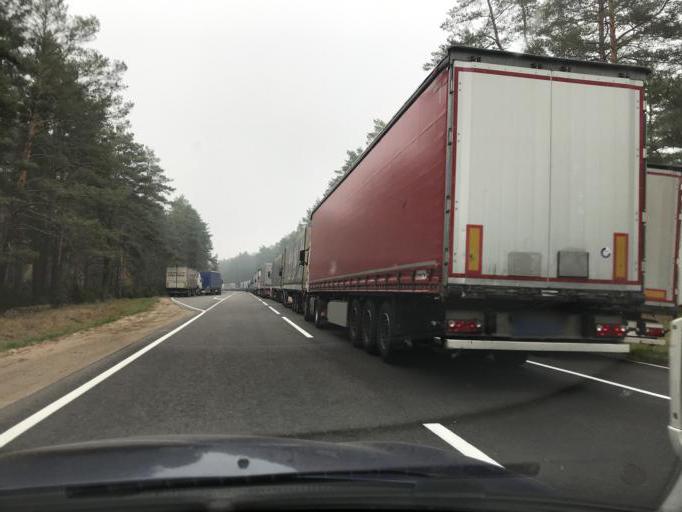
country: LT
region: Alytaus apskritis
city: Druskininkai
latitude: 53.9342
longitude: 23.9478
